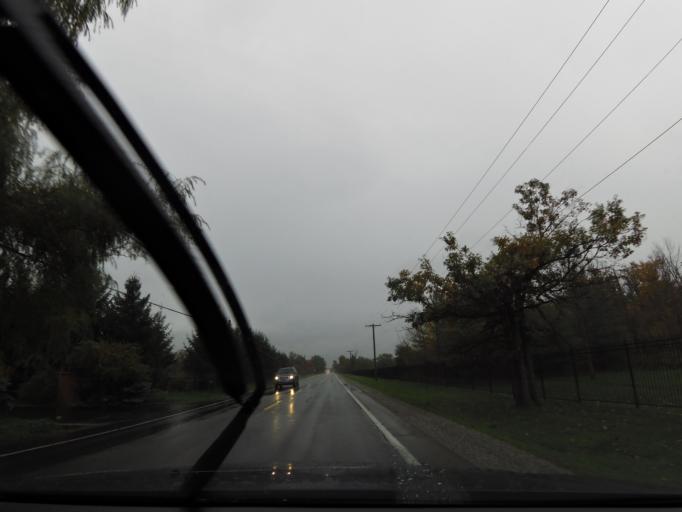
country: CA
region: Ontario
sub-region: Halton
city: Milton
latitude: 43.4515
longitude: -79.8833
